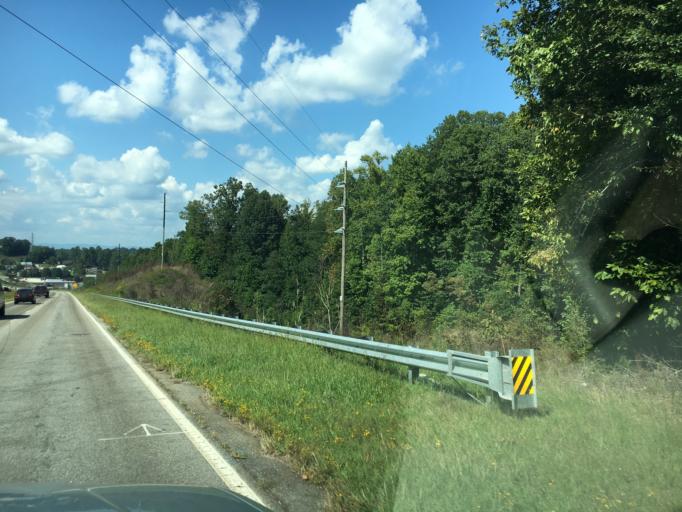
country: US
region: South Carolina
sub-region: Anderson County
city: Powdersville
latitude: 34.8167
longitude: -82.5186
